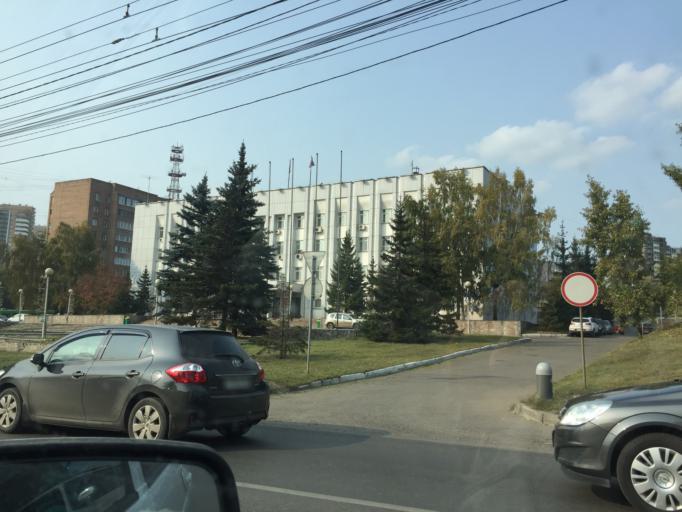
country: RU
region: Krasnoyarskiy
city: Krasnoyarsk
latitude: 56.0333
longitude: 92.9229
